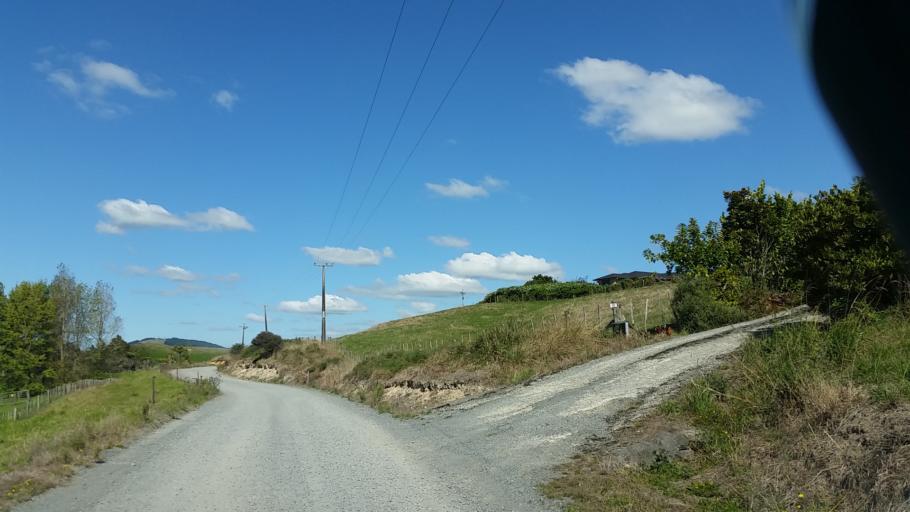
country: NZ
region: Northland
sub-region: Whangarei
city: Maungatapere
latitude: -35.6902
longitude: 174.2276
